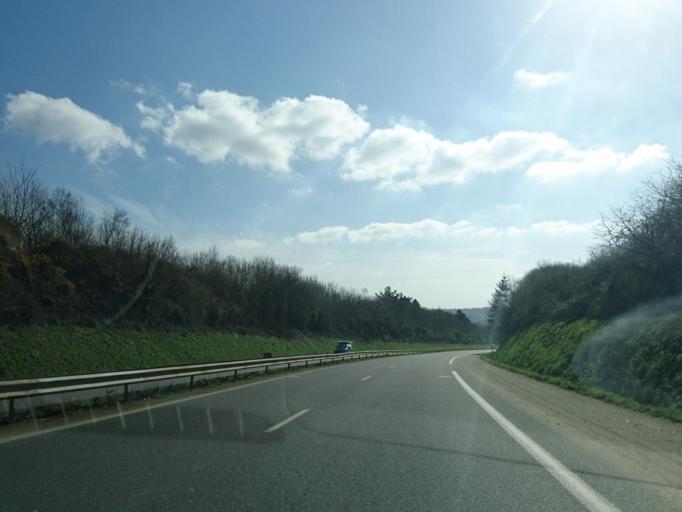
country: FR
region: Brittany
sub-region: Departement du Finistere
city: Le Relecq-Kerhuon
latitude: 48.4092
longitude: -4.4153
